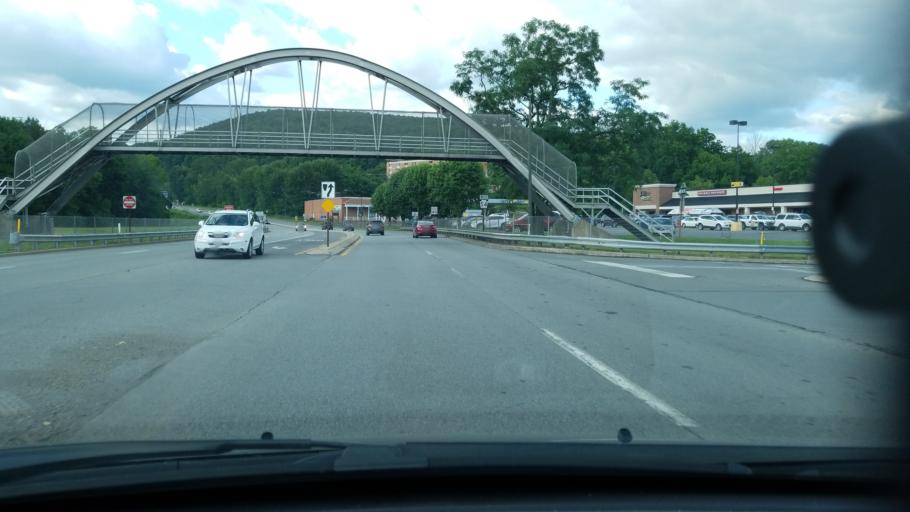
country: US
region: Pennsylvania
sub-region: Montour County
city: Danville
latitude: 40.9660
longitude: -76.6168
